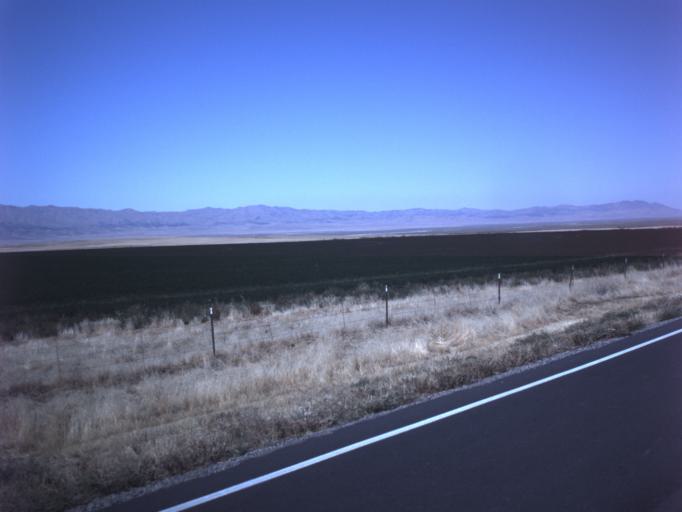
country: US
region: Utah
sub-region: Tooele County
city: Grantsville
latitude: 40.4365
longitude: -112.7487
